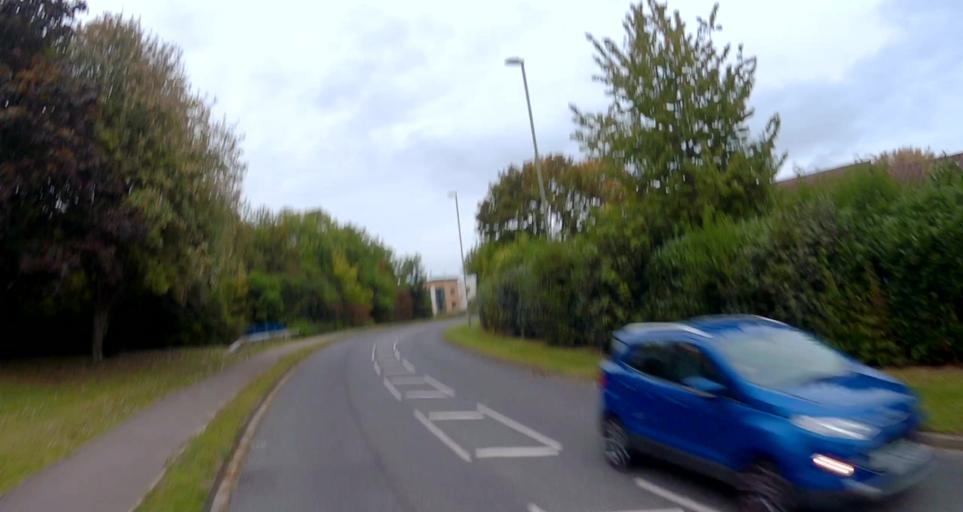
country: GB
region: England
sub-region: Hampshire
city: Basingstoke
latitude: 51.2423
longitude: -1.1173
